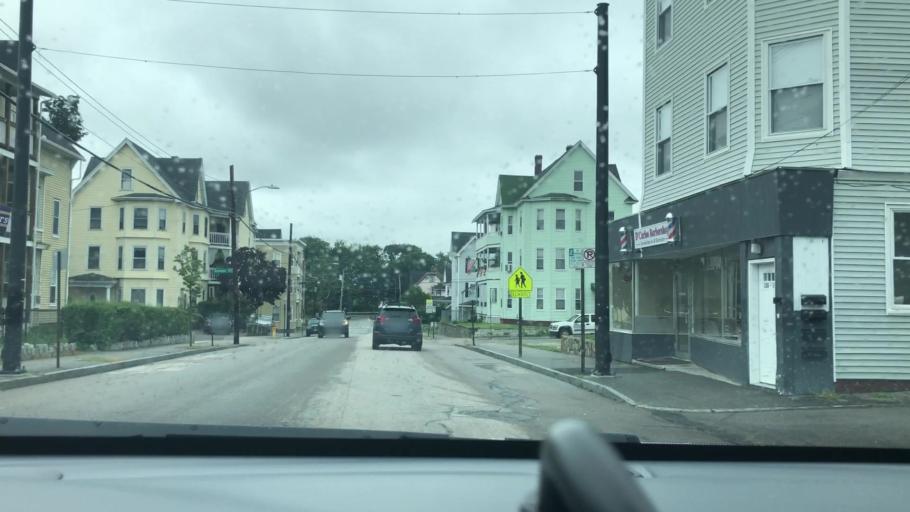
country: US
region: New Hampshire
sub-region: Hillsborough County
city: Manchester
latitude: 42.9953
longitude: -71.4783
